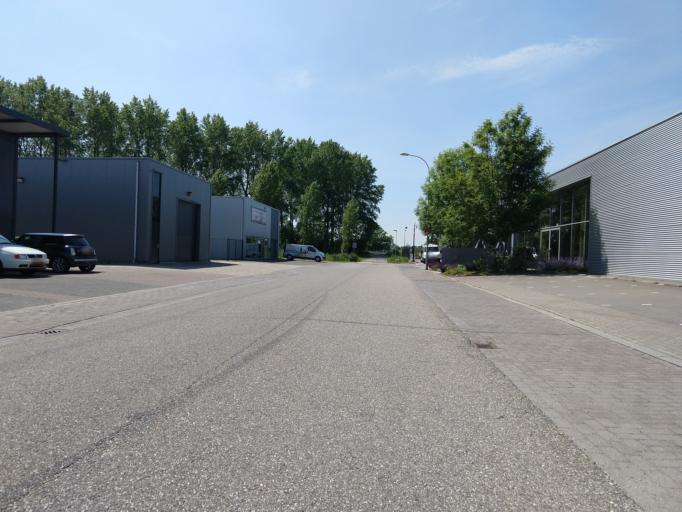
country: NL
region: Zeeland
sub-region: Gemeente Goes
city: Goes
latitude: 51.4819
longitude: 3.8132
